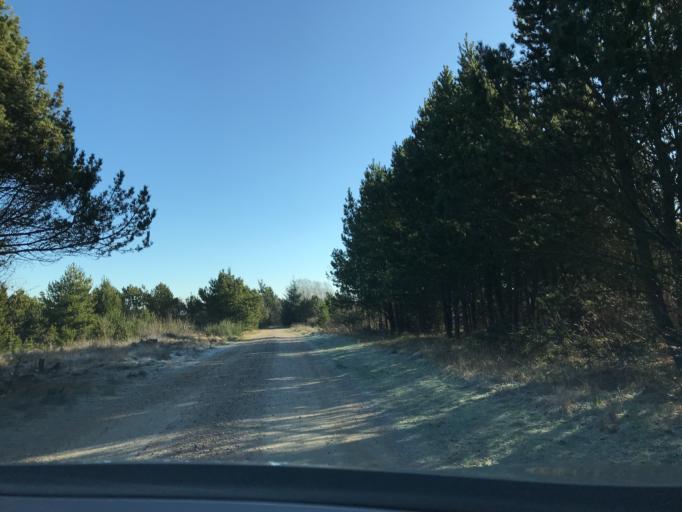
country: DK
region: South Denmark
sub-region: Varde Kommune
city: Oksbol
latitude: 55.7758
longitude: 8.2442
